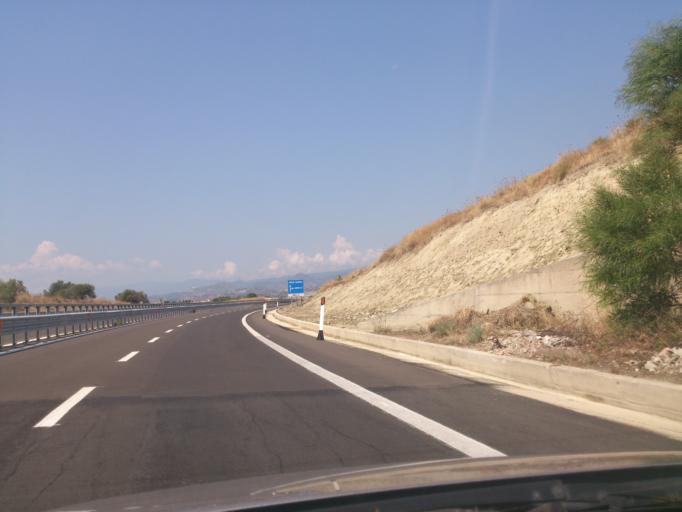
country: IT
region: Calabria
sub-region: Provincia di Reggio Calabria
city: Roccella Ionica
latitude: 38.3113
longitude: 16.3620
